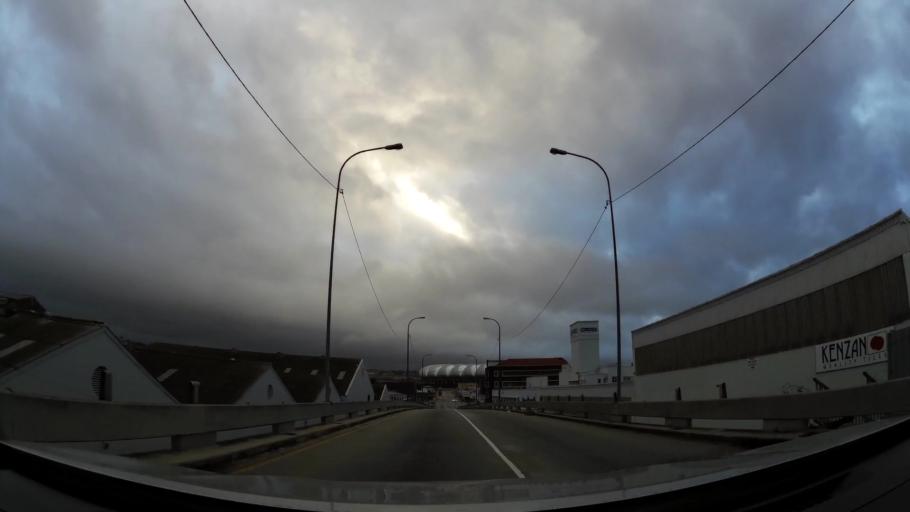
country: ZA
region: Eastern Cape
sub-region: Nelson Mandela Bay Metropolitan Municipality
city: Port Elizabeth
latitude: -33.9377
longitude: 25.6078
